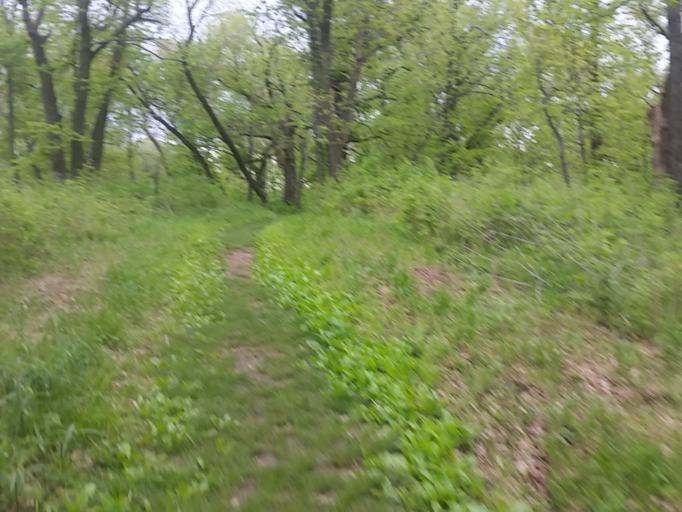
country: US
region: Nebraska
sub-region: Sarpy County
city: Bellevue
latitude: 41.1788
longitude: -95.9084
